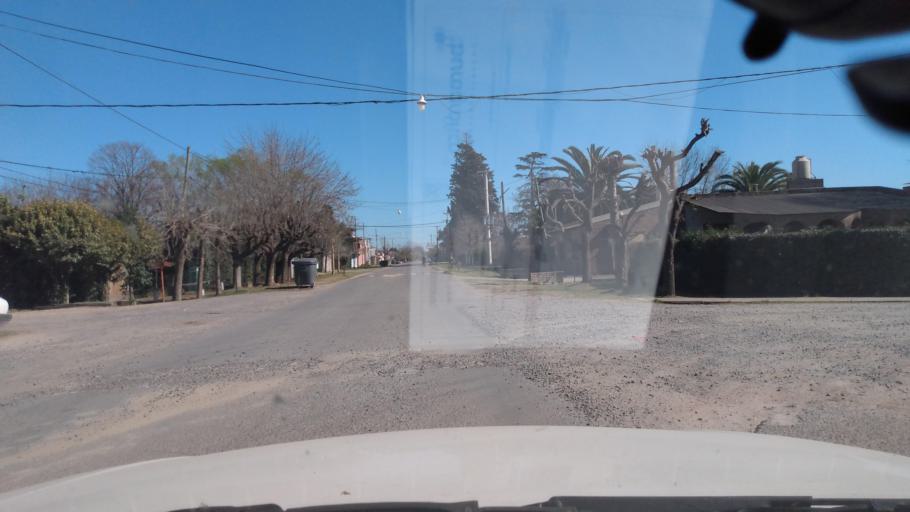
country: AR
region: Buenos Aires
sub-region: Partido de Mercedes
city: Mercedes
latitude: -34.6578
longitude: -59.4071
